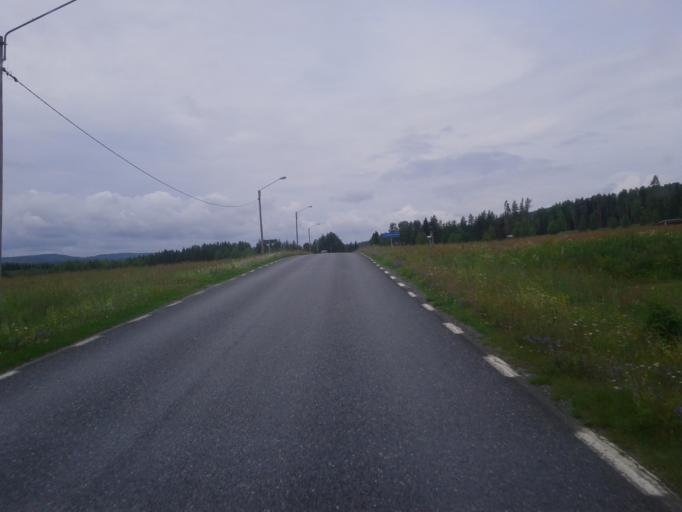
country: SE
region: Vaesterbotten
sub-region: Skelleftea Kommun
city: Forsbacka
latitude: 64.9070
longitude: 20.6278
